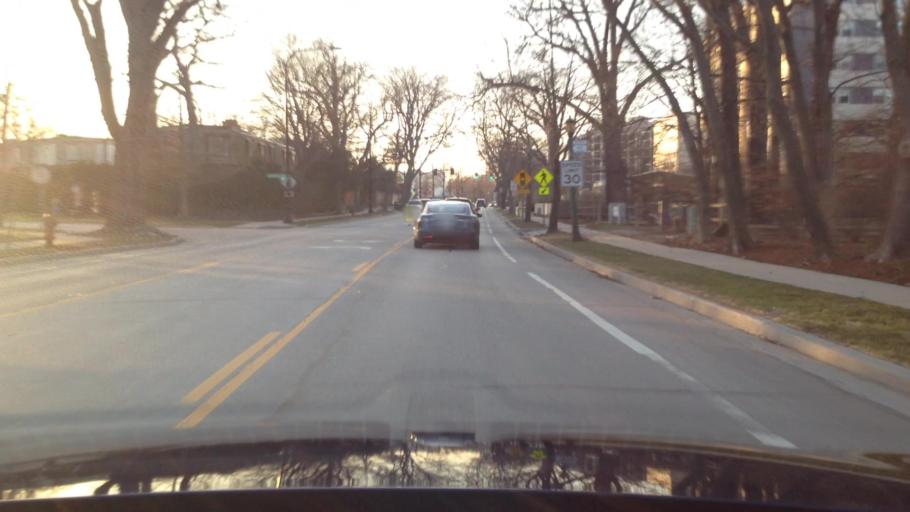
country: US
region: Illinois
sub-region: Cook County
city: Kenilworth
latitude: 42.0849
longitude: -87.6978
